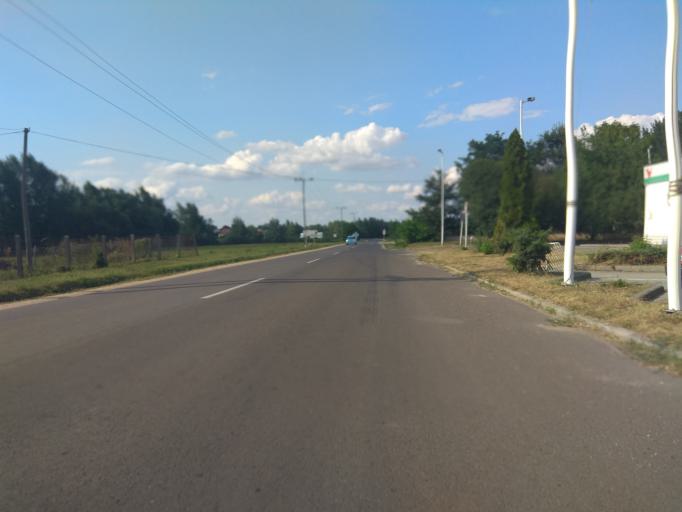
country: HU
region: Borsod-Abauj-Zemplen
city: Mezocsat
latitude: 47.8364
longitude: 20.9004
